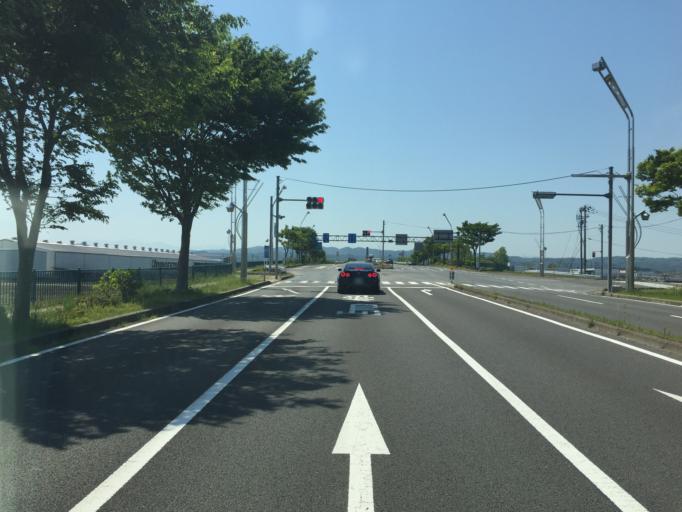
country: JP
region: Miyagi
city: Iwanuma
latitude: 38.1389
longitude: 140.8842
